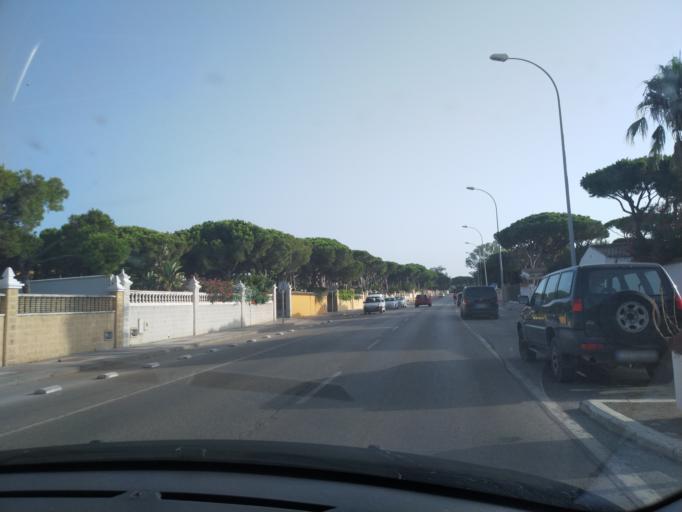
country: ES
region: Andalusia
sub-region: Provincia de Cadiz
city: Chiclana de la Frontera
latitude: 36.3830
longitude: -6.1900
